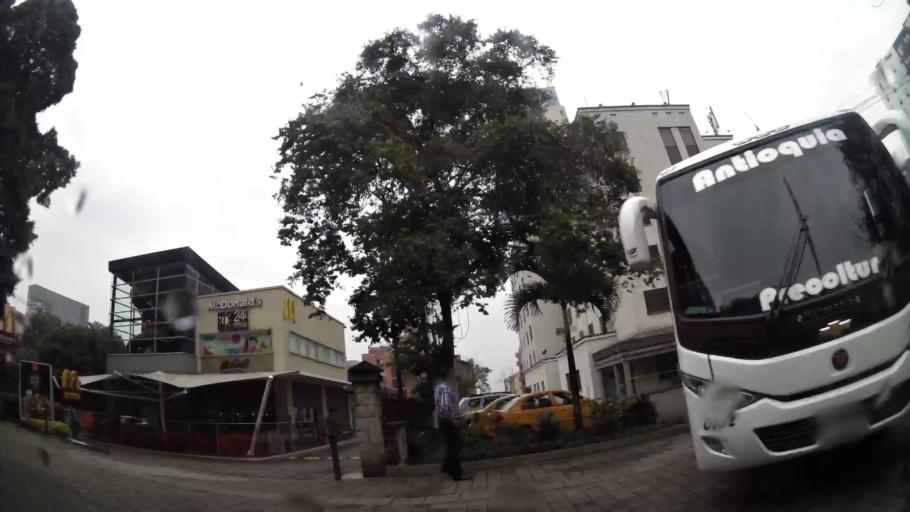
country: CO
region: Antioquia
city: Itagui
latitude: 6.1996
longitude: -75.5736
